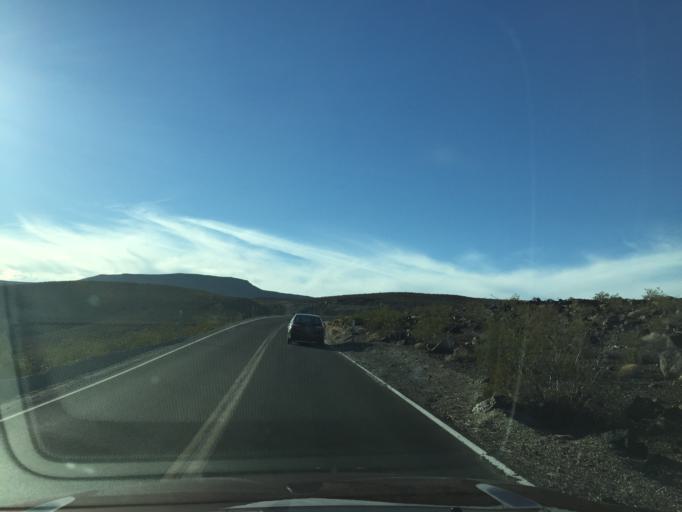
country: US
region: California
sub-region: Inyo County
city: Lone Pine
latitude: 36.3469
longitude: -117.5416
